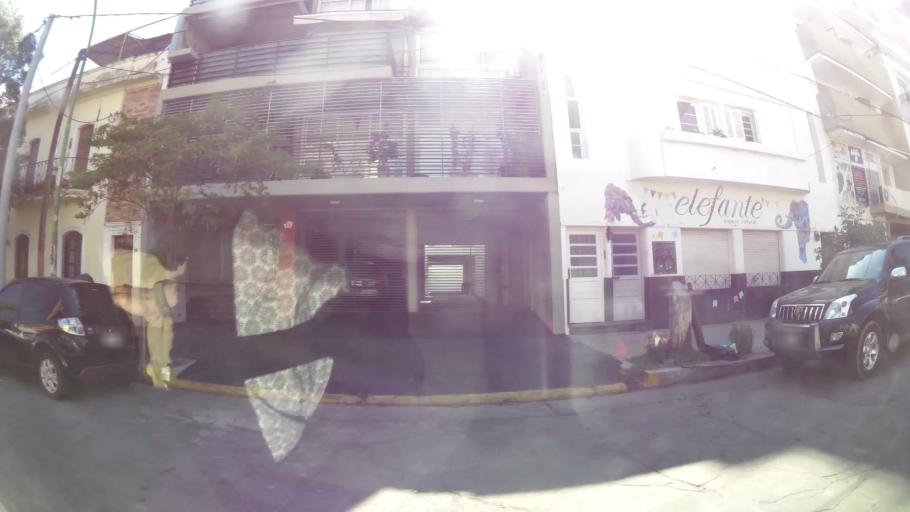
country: AR
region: Cordoba
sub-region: Departamento de Capital
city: Cordoba
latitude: -31.4158
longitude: -64.1666
